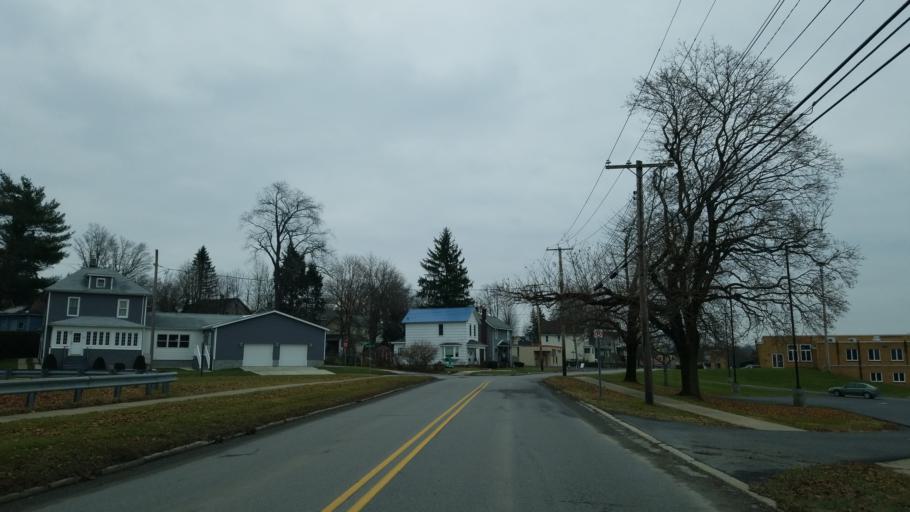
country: US
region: Pennsylvania
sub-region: Clearfield County
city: DuBois
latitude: 41.1314
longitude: -78.7575
